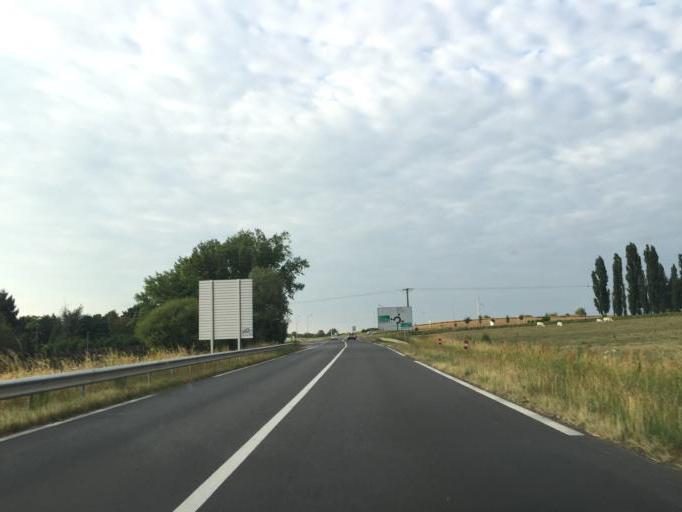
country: FR
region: Auvergne
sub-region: Departement de l'Allier
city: Varennes-sur-Allier
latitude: 46.3020
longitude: 3.4253
